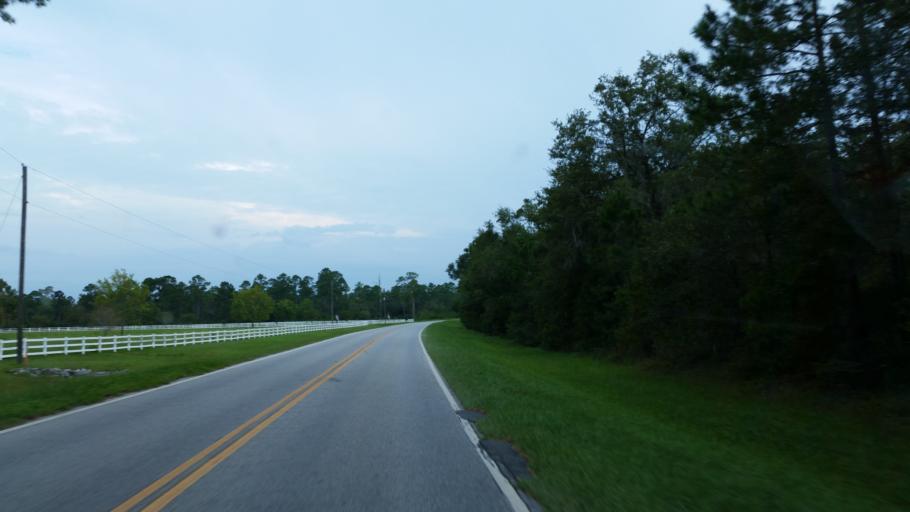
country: US
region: Georgia
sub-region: Lowndes County
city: Valdosta
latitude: 30.7586
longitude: -83.3047
